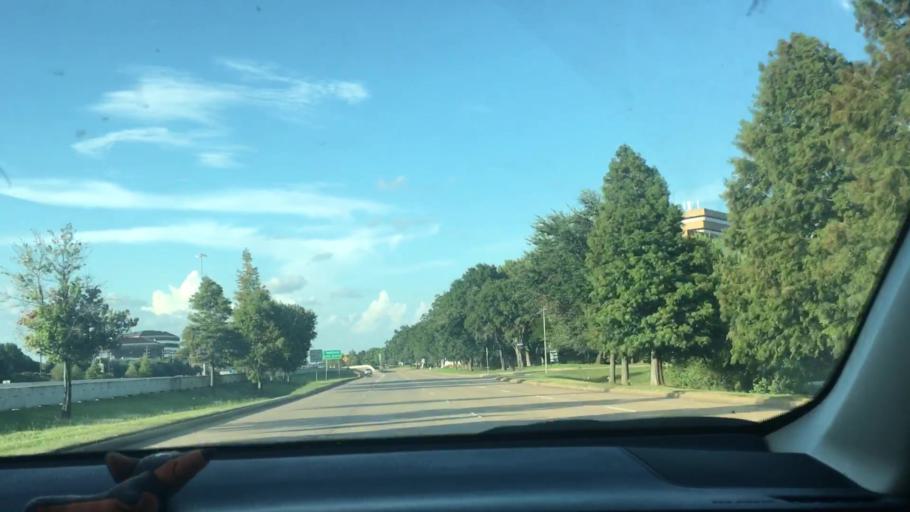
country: US
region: Texas
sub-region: Fort Bend County
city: Sugar Land
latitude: 29.6121
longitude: -95.6084
